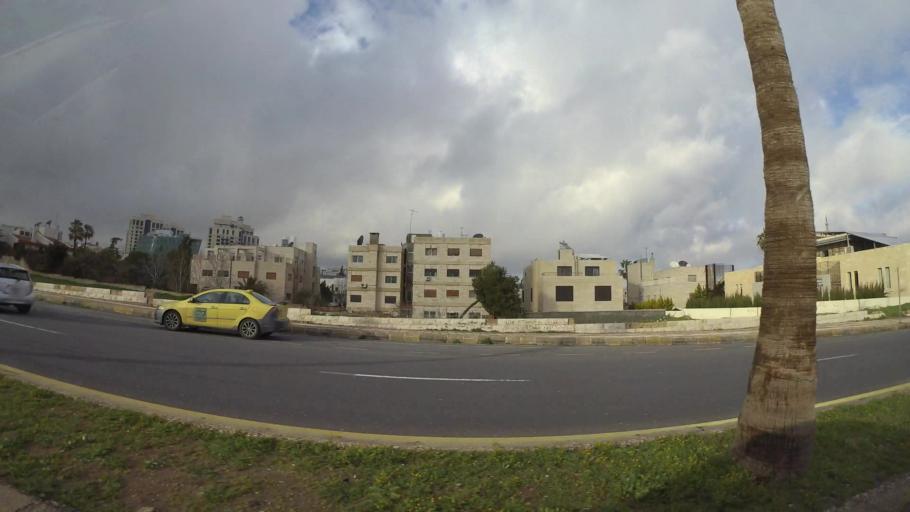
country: JO
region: Amman
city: Wadi as Sir
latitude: 31.9535
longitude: 35.8788
